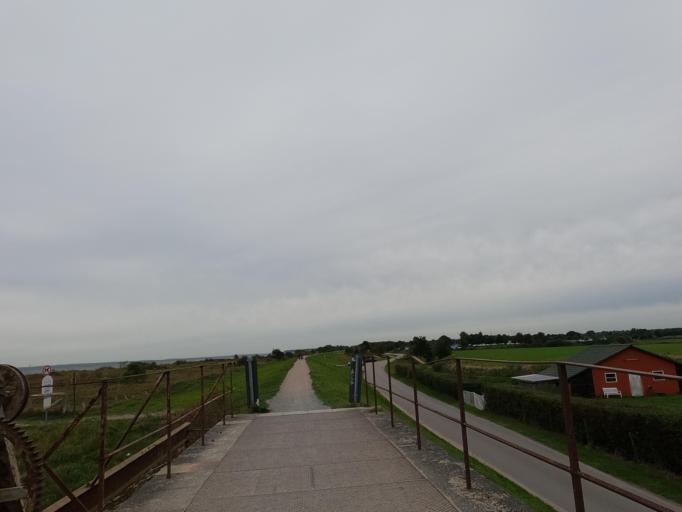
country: DE
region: Schleswig-Holstein
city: Gromitz
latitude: 54.1648
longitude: 11.0130
